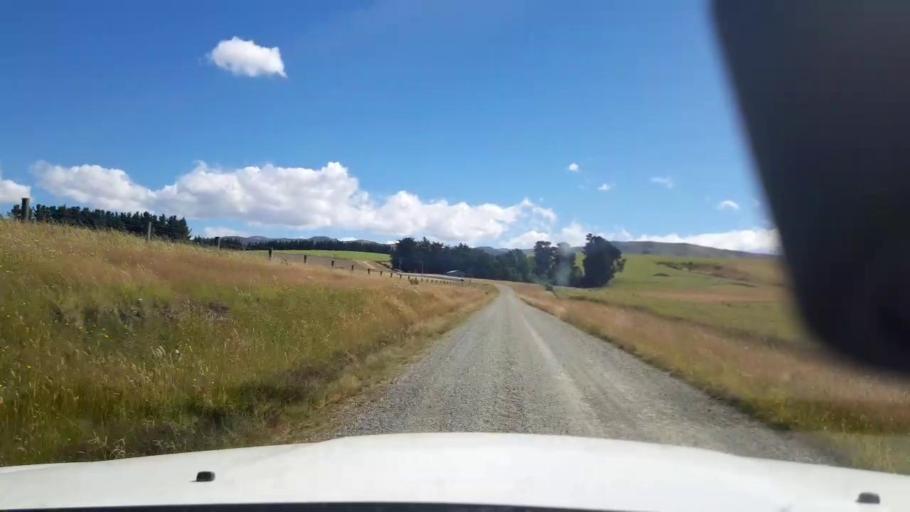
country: NZ
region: Canterbury
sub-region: Timaru District
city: Pleasant Point
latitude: -44.3145
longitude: 170.8905
